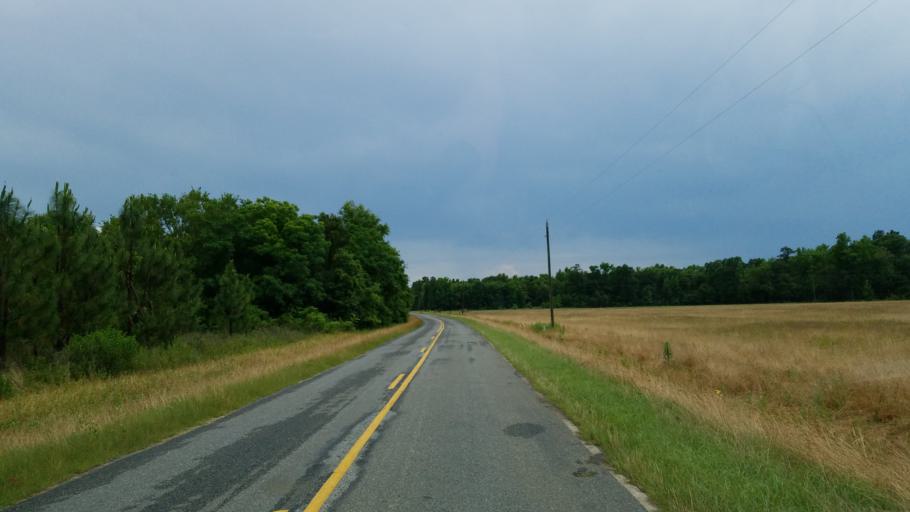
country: US
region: Georgia
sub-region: Dooly County
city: Unadilla
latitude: 32.2700
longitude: -83.7968
